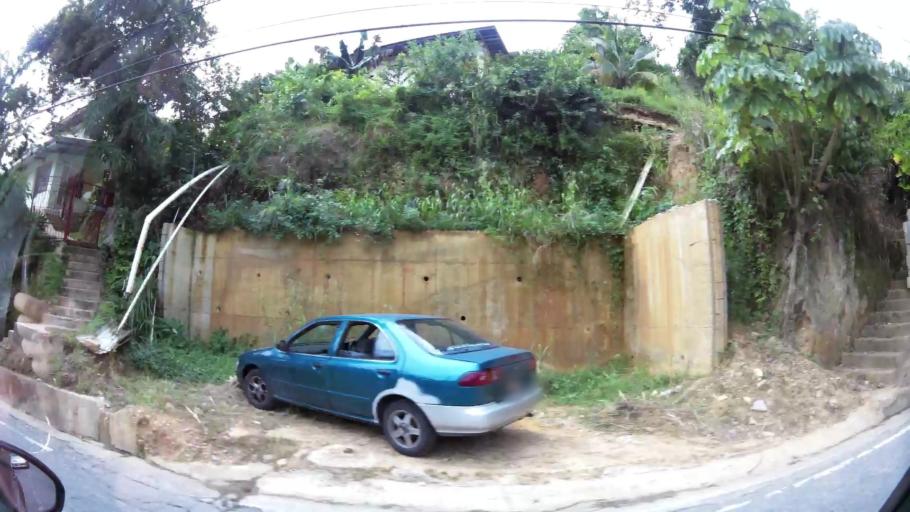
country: TT
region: Diego Martin
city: Petit Valley
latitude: 10.7116
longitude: -61.5154
